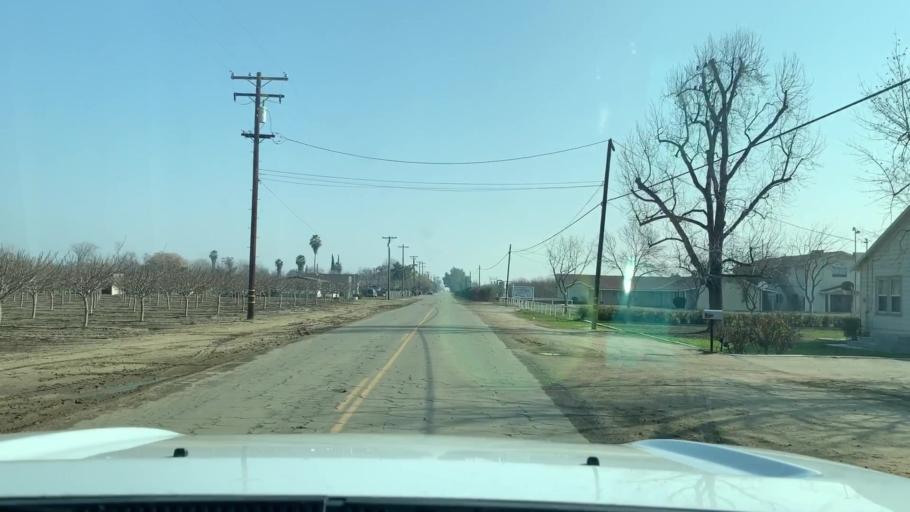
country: US
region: California
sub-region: Kern County
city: Shafter
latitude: 35.4781
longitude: -119.2844
